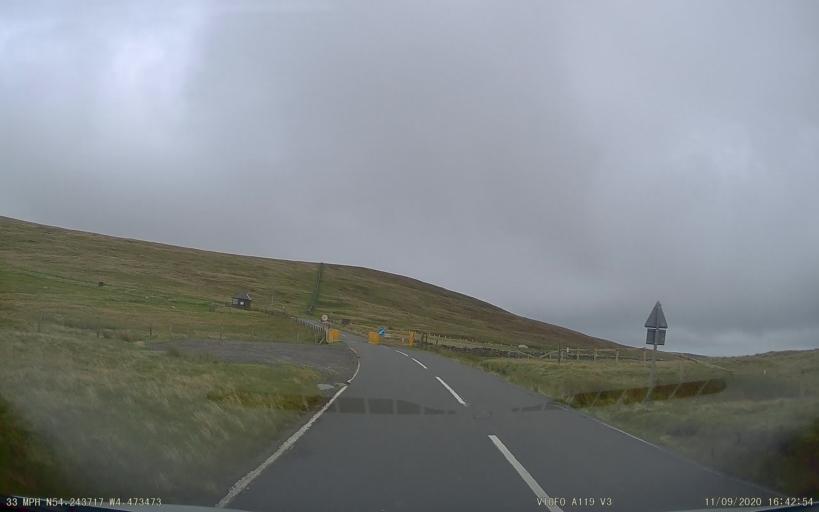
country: IM
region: Laxey
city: Laxey
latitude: 54.2437
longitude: -4.4731
